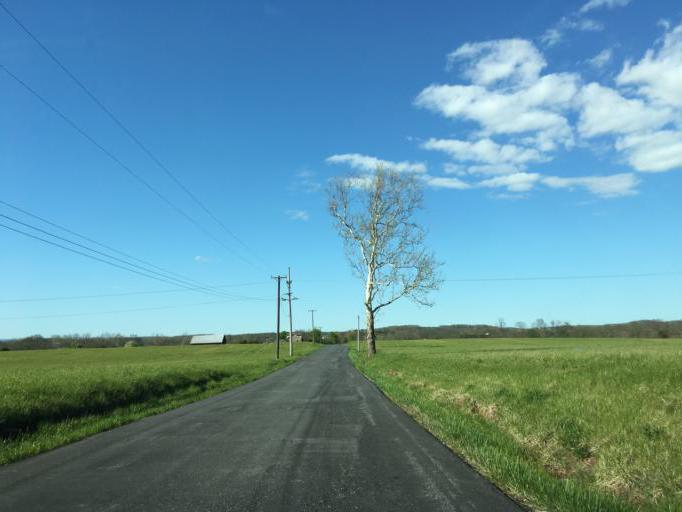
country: US
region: Maryland
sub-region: Frederick County
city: Emmitsburg
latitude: 39.6850
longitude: -77.3208
